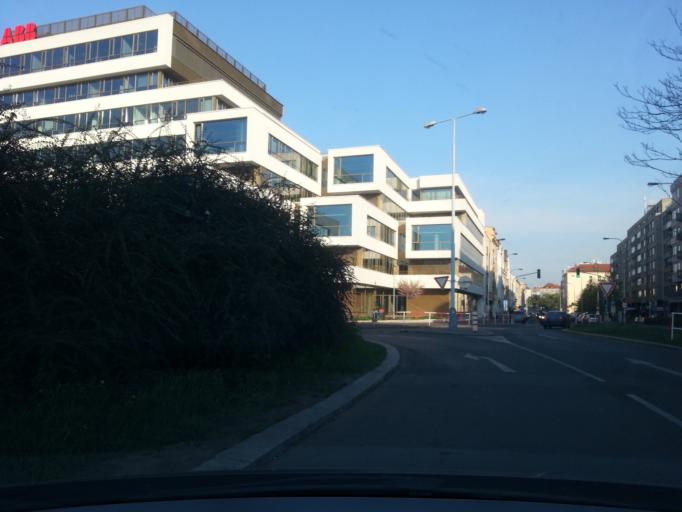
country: CZ
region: Praha
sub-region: Praha 2
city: Vysehrad
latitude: 50.0599
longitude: 14.4292
